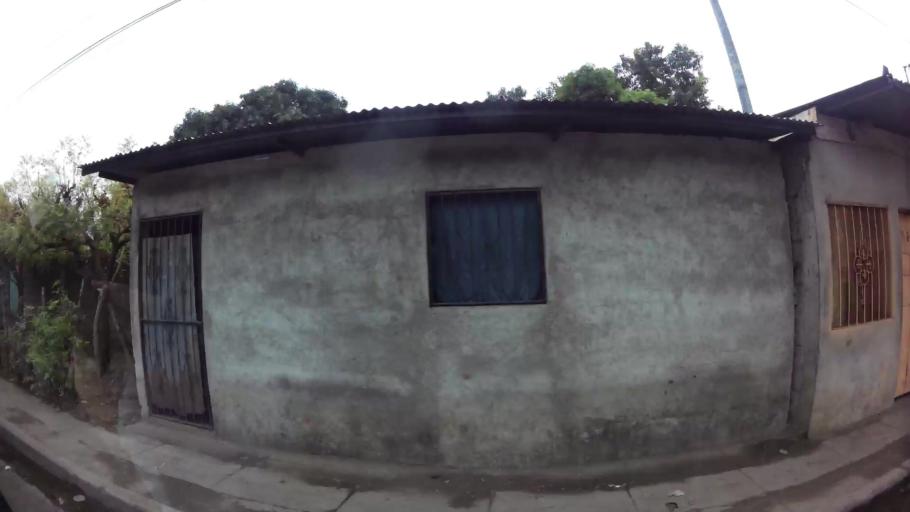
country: NI
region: Chinandega
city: Chinandega
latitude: 12.6176
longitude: -87.1180
